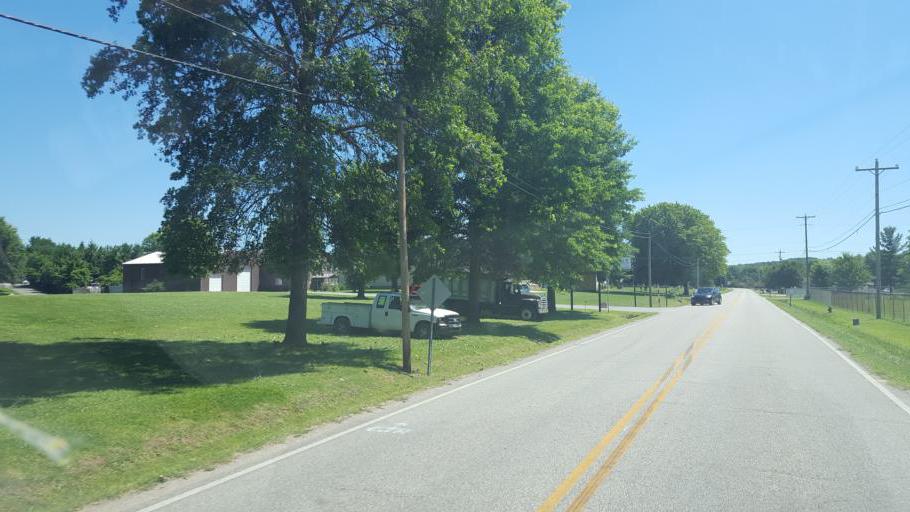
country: US
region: West Virginia
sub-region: Cabell County
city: Pea Ridge
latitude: 38.4435
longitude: -82.3389
